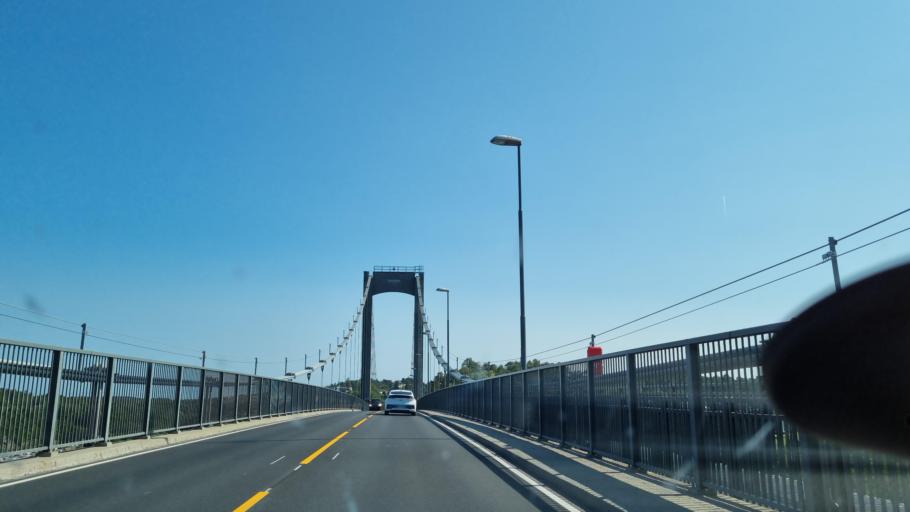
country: NO
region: Aust-Agder
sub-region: Arendal
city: Arendal
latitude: 58.4714
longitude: 8.8228
